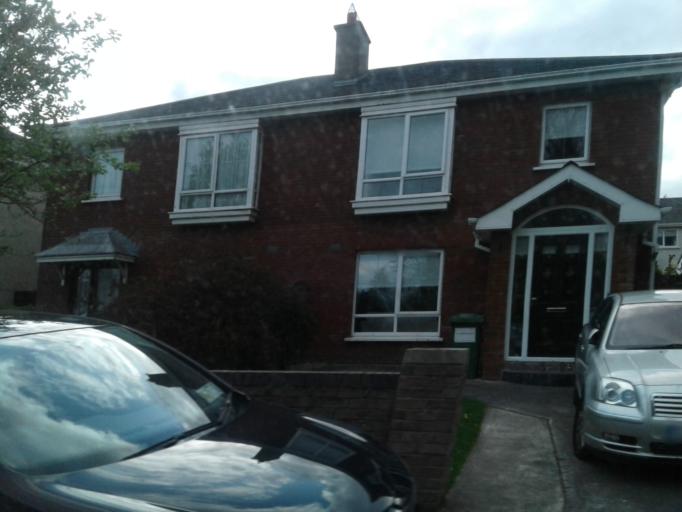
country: IE
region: Leinster
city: Beaumont
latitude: 53.3902
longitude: -6.2291
